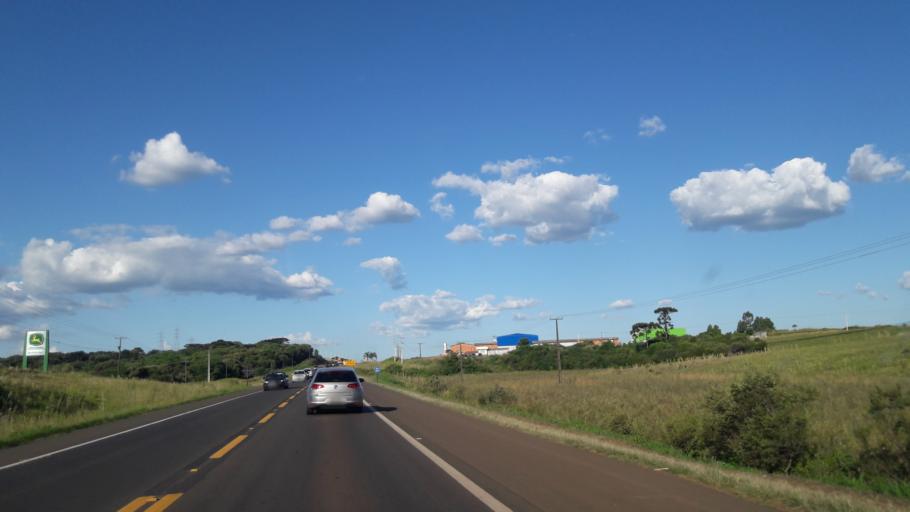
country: BR
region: Parana
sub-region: Guarapuava
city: Guarapuava
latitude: -25.3751
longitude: -51.5024
